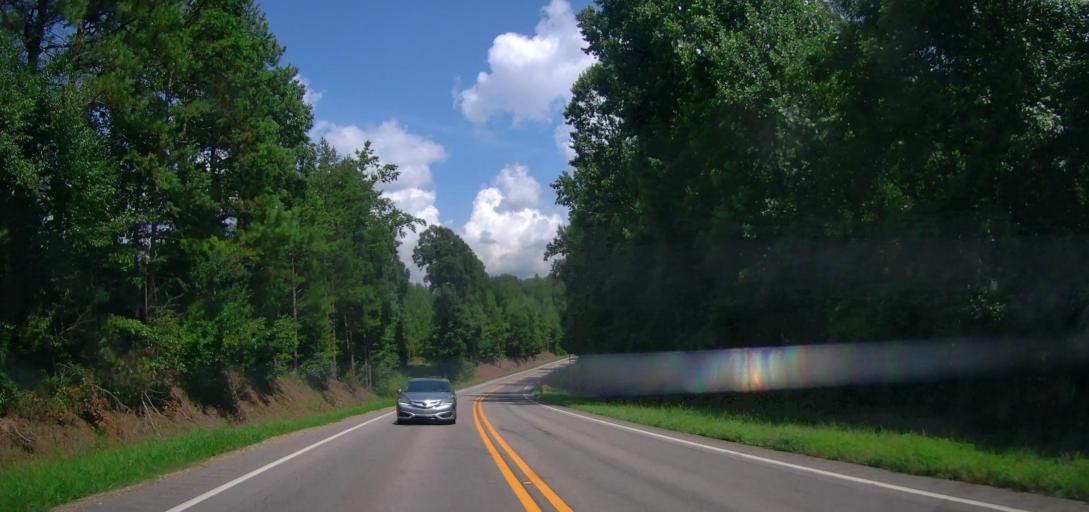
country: US
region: Alabama
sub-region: Cleburne County
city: Heflin
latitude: 33.6413
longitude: -85.4923
